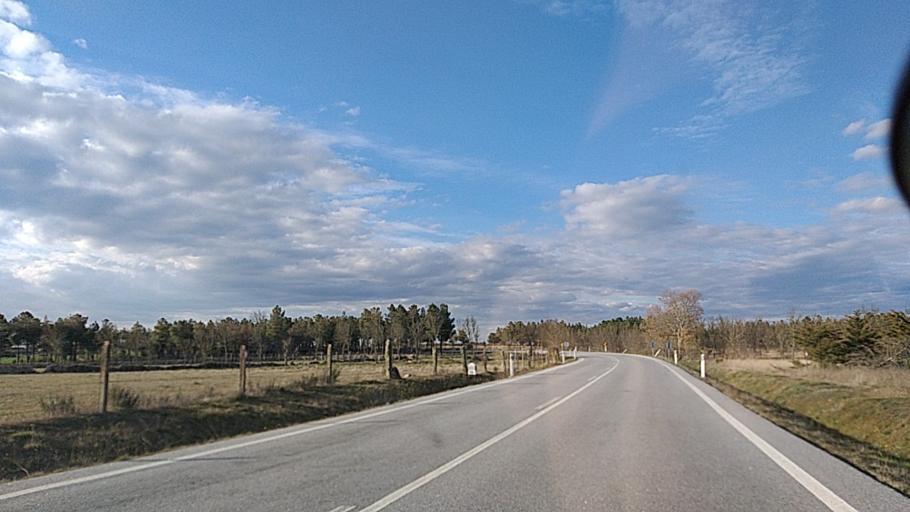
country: ES
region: Castille and Leon
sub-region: Provincia de Salamanca
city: Aldea del Obispo
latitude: 40.6686
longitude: -6.8589
